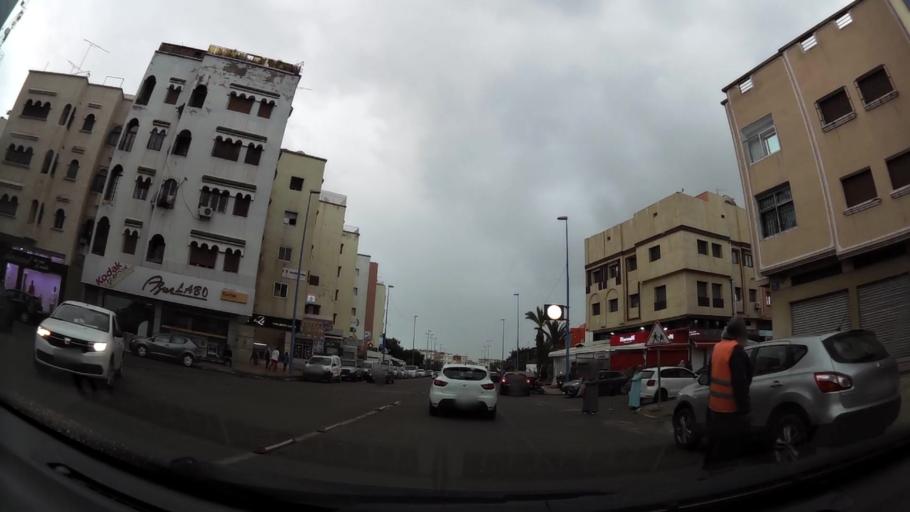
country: MA
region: Grand Casablanca
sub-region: Casablanca
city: Casablanca
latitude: 33.5520
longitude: -7.6022
